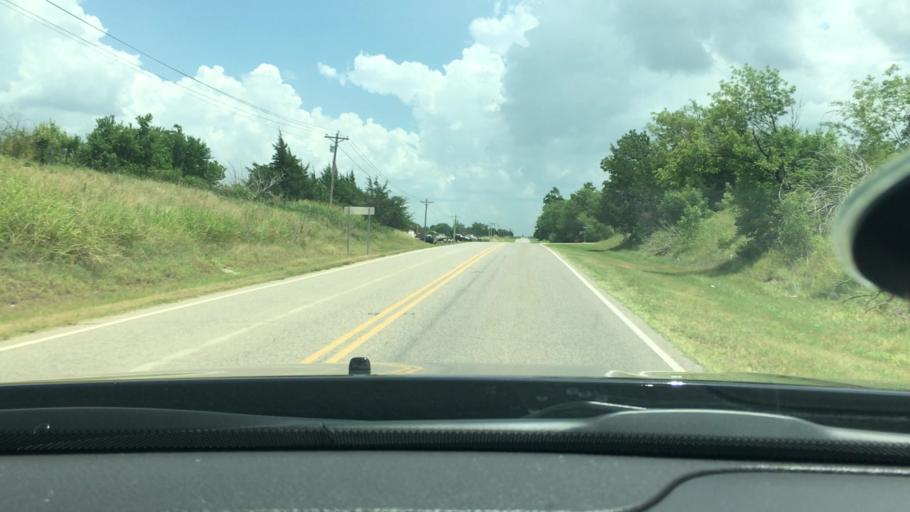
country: US
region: Oklahoma
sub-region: Love County
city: Marietta
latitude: 33.9403
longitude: -97.0889
